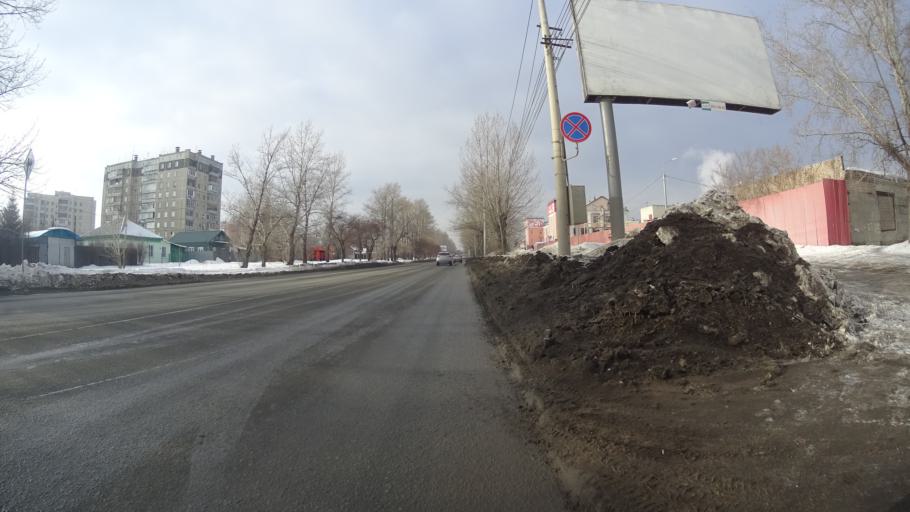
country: RU
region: Chelyabinsk
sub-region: Gorod Chelyabinsk
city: Chelyabinsk
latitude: 55.1223
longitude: 61.3762
